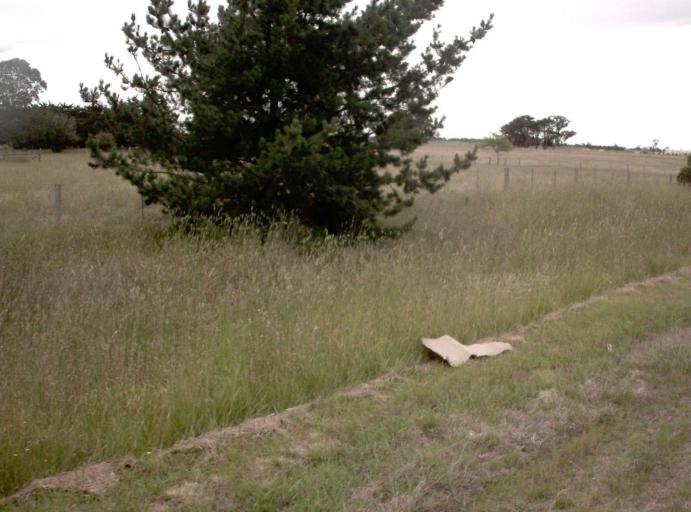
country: AU
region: Victoria
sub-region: Wellington
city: Sale
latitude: -38.0733
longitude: 147.1165
